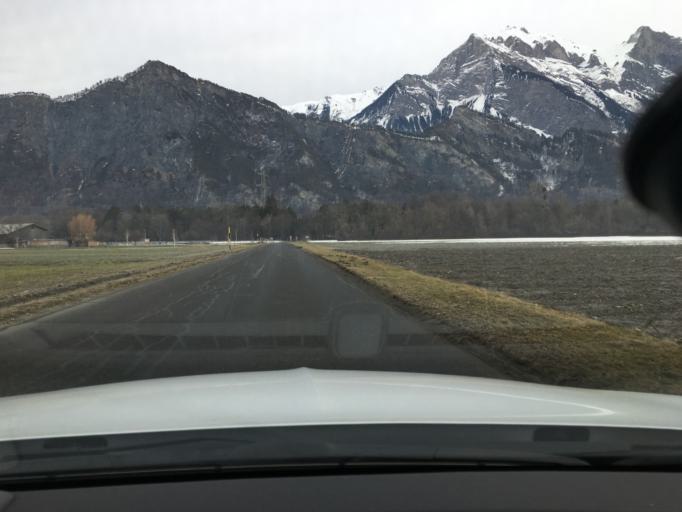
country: CH
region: Saint Gallen
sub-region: Wahlkreis Sarganserland
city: Bad Ragaz
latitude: 47.0188
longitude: 9.4957
